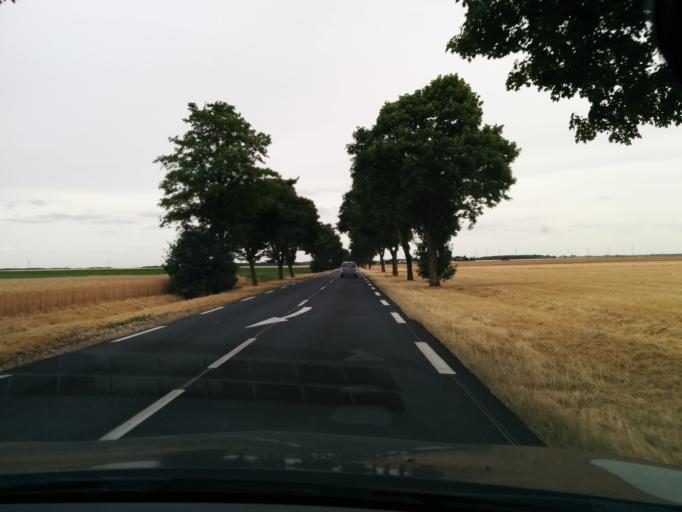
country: FR
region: Ile-de-France
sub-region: Departement de l'Essonne
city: Pussay
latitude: 48.3865
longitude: 1.9751
